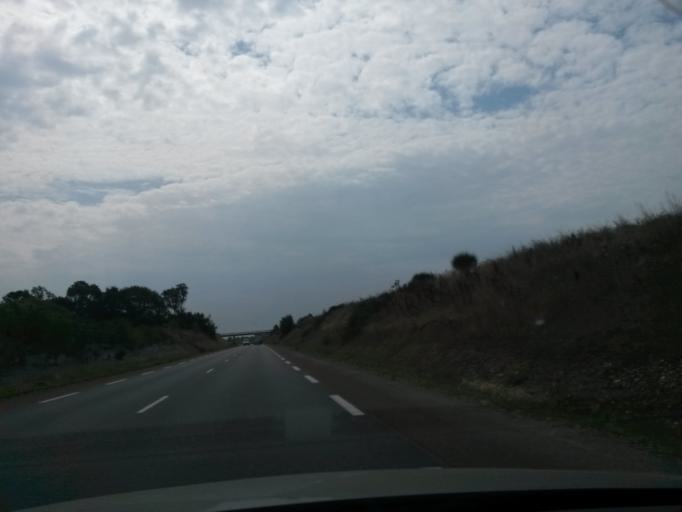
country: FR
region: Poitou-Charentes
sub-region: Departement de la Charente-Maritime
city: Saint-Xandre
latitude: 46.1880
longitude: -1.0938
